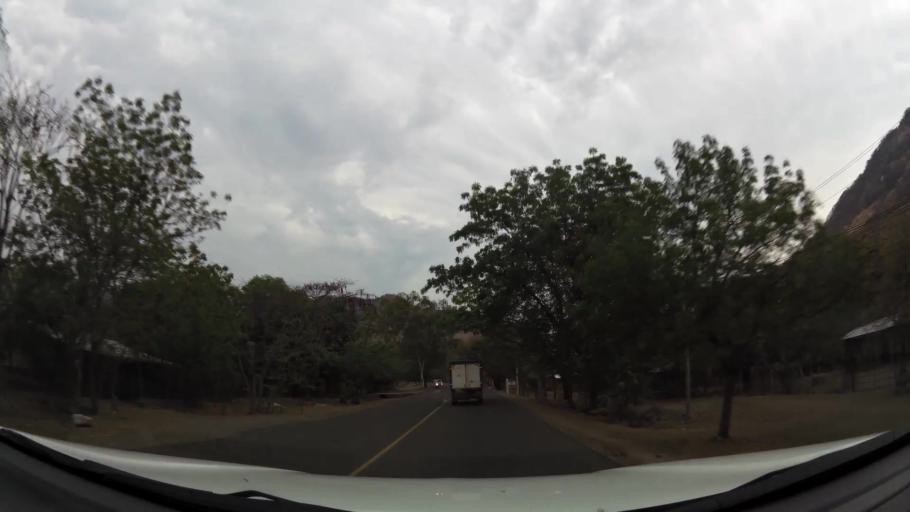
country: NI
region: Leon
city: Santa Rosa del Penon
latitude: 12.9373
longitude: -86.2055
